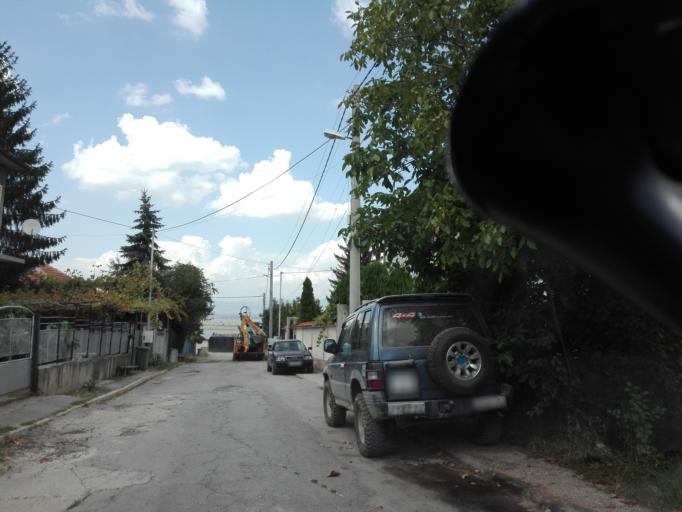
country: BG
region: Sofiya
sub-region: Obshtina Elin Pelin
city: Elin Pelin
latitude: 42.6044
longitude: 23.4819
